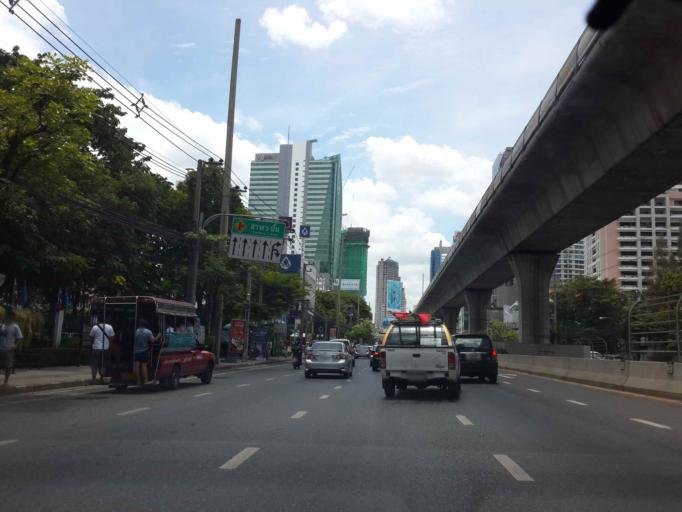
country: TH
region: Bangkok
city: Bang Rak
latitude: 13.7202
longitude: 100.5252
